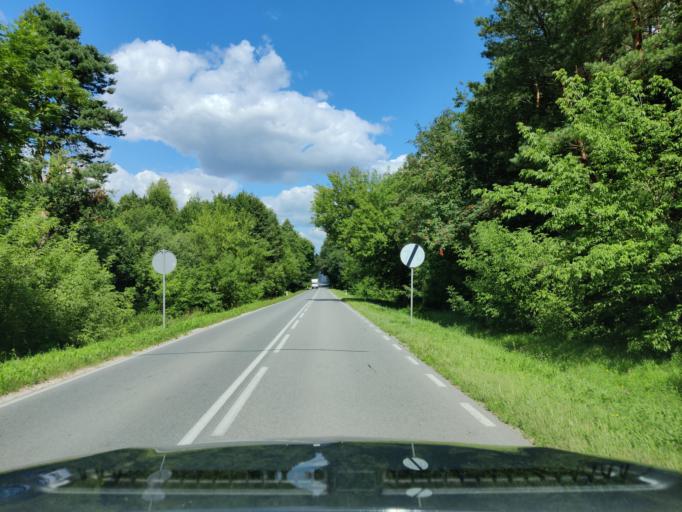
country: PL
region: Masovian Voivodeship
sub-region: Powiat wegrowski
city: Grebkow
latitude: 52.2239
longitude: 21.8773
